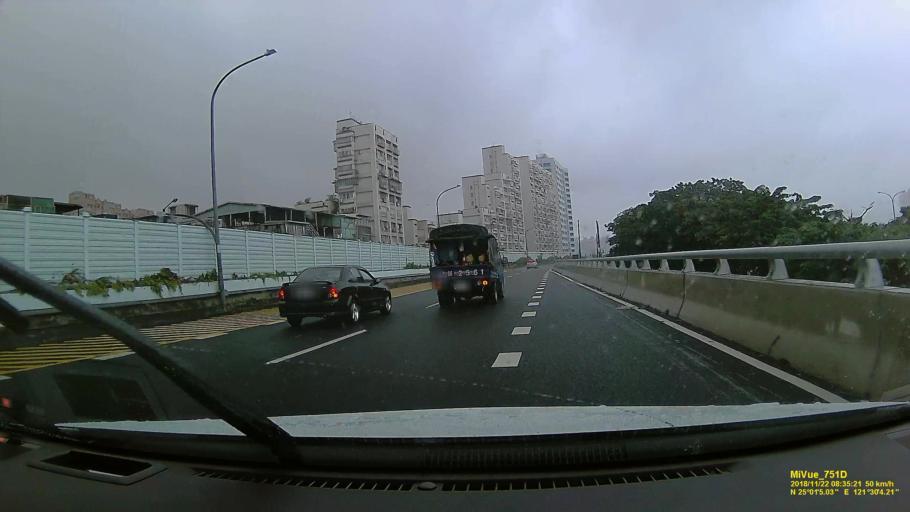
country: TW
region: Taipei
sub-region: Taipei
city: Banqiao
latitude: 25.0181
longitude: 121.5013
